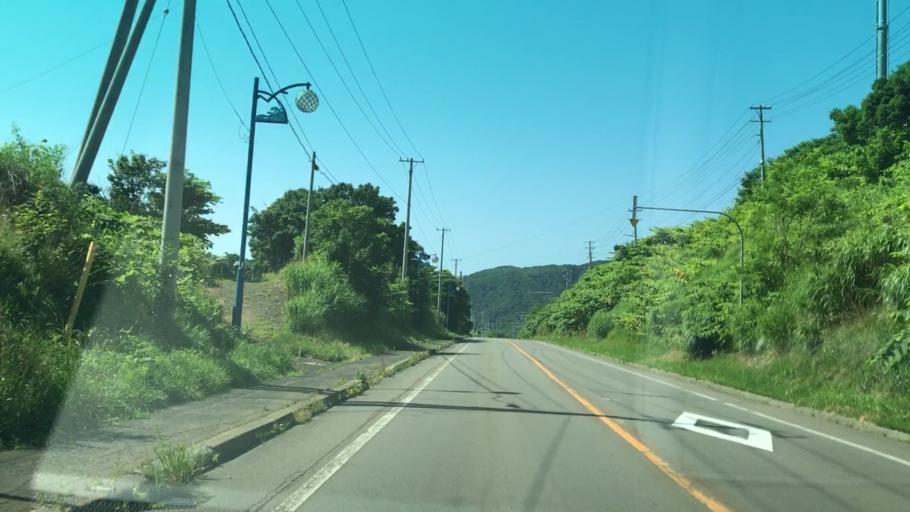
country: JP
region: Hokkaido
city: Iwanai
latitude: 43.0686
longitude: 140.4933
